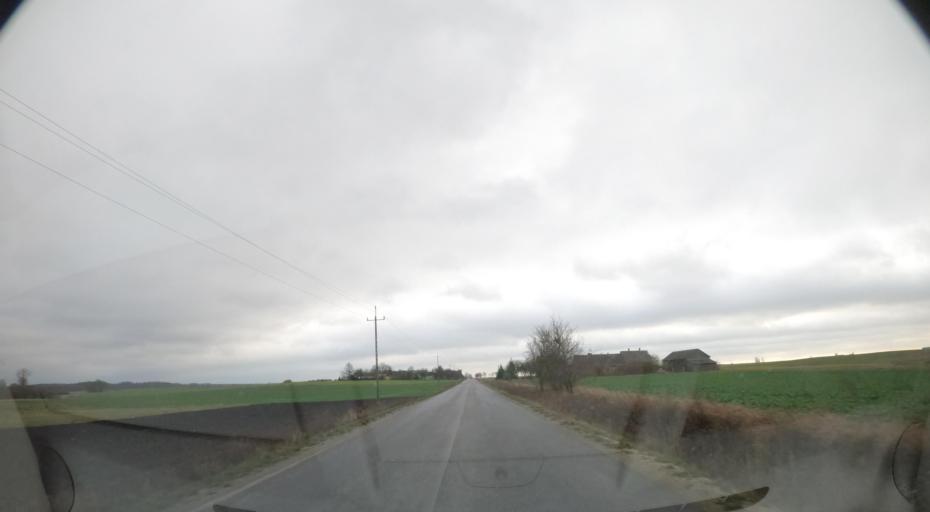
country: PL
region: Greater Poland Voivodeship
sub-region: Powiat pilski
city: Lobzenica
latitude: 53.2193
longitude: 17.3432
